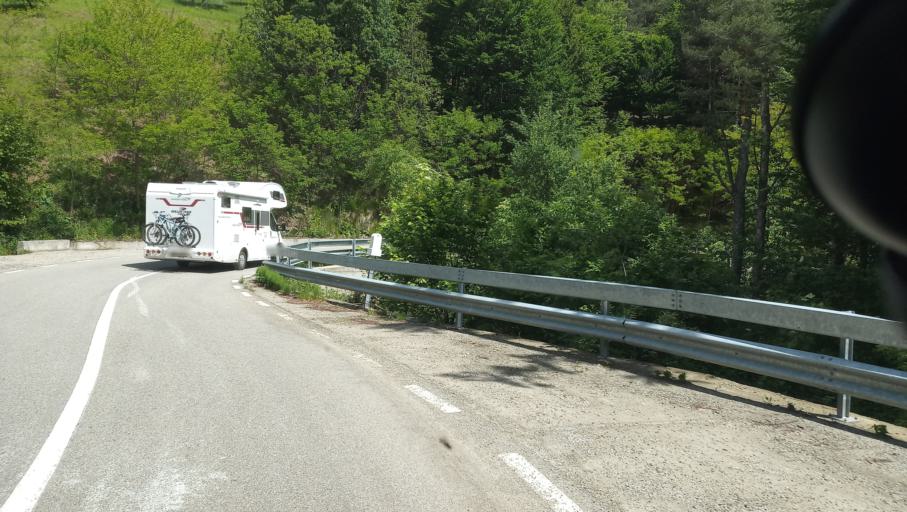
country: RO
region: Caras-Severin
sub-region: Comuna Brebu Nou
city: Brebu Nou
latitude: 45.2510
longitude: 22.1777
